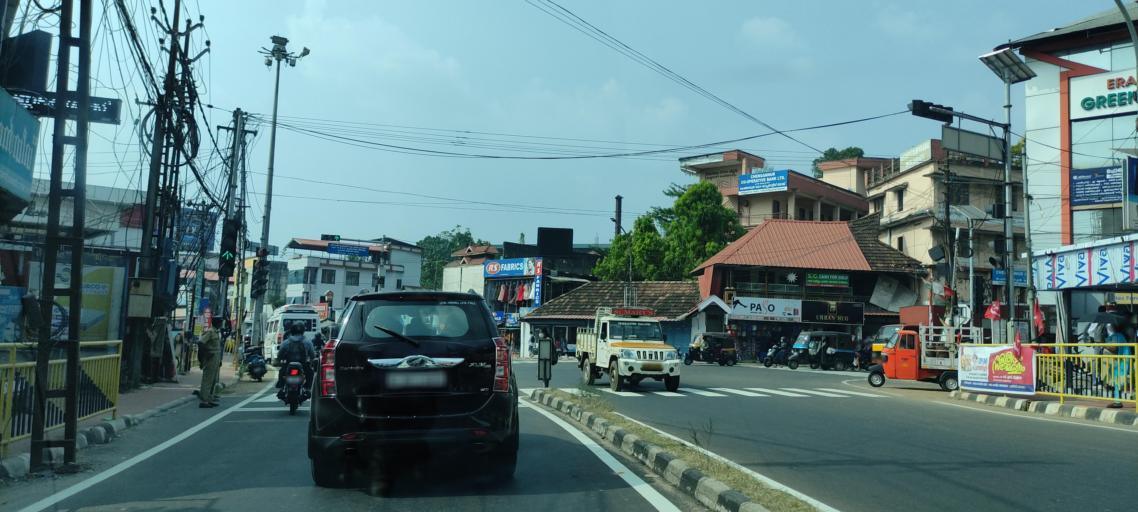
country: IN
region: Kerala
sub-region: Alappuzha
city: Chengannur
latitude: 9.3176
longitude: 76.6159
